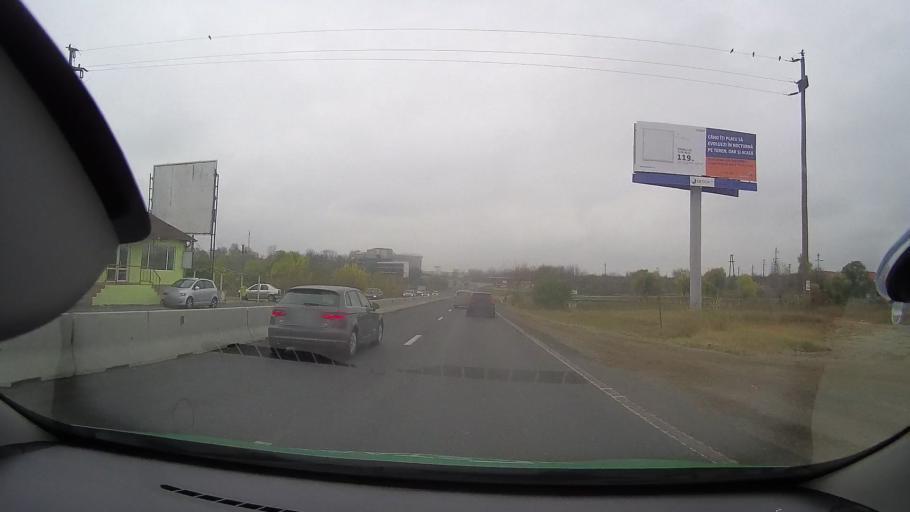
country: RO
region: Ilfov
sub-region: Comuna Ciolpani
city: Ciolpani
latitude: 44.6750
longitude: 26.0744
